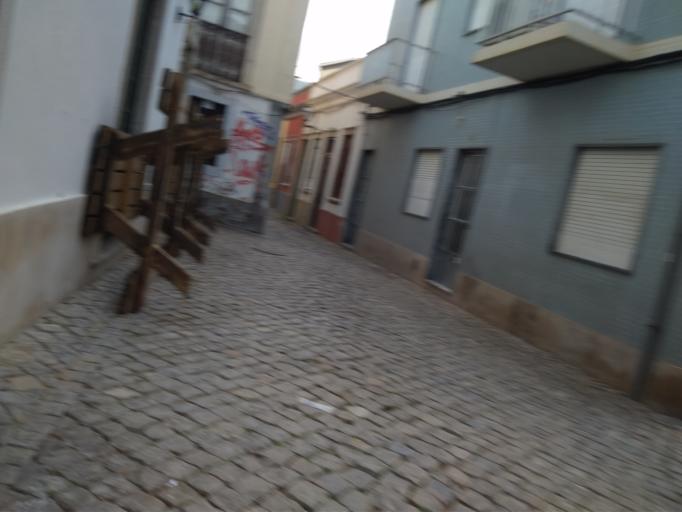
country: PT
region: Faro
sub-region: Faro
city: Faro
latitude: 37.0174
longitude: -7.9349
